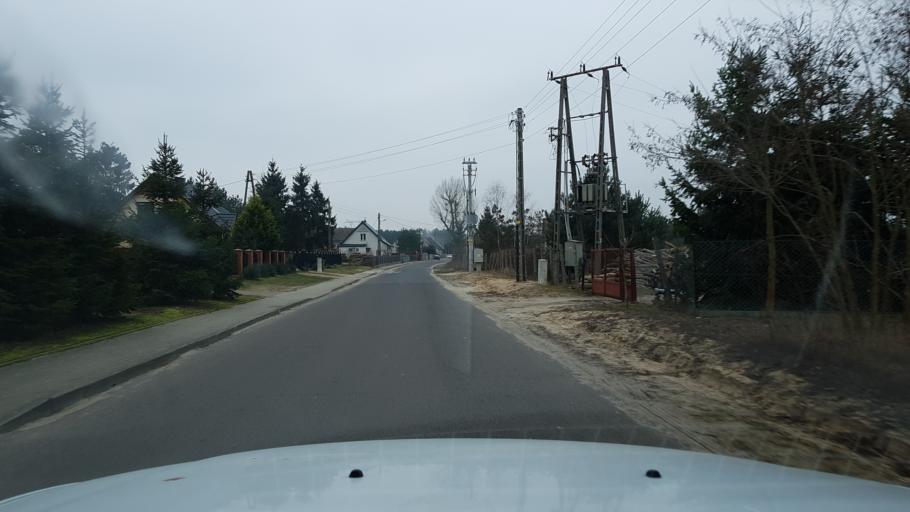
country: PL
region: West Pomeranian Voivodeship
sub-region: Powiat gryfinski
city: Gryfino
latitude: 53.1988
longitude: 14.4980
